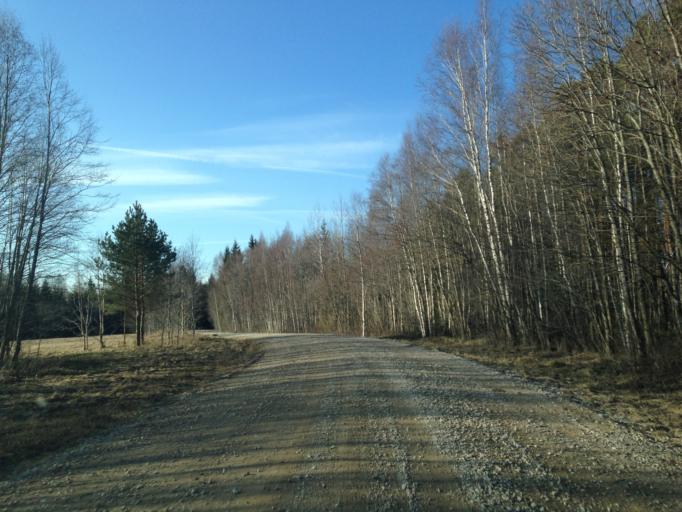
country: EE
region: Harju
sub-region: Nissi vald
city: Turba
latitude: 59.1685
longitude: 24.1395
